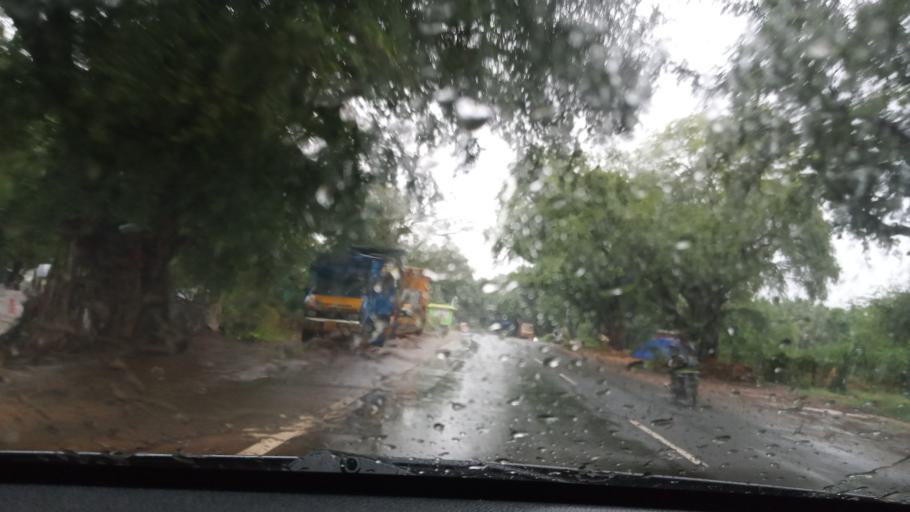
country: IN
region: Tamil Nadu
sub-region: Vellore
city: Kalavai
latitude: 12.8038
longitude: 79.4294
